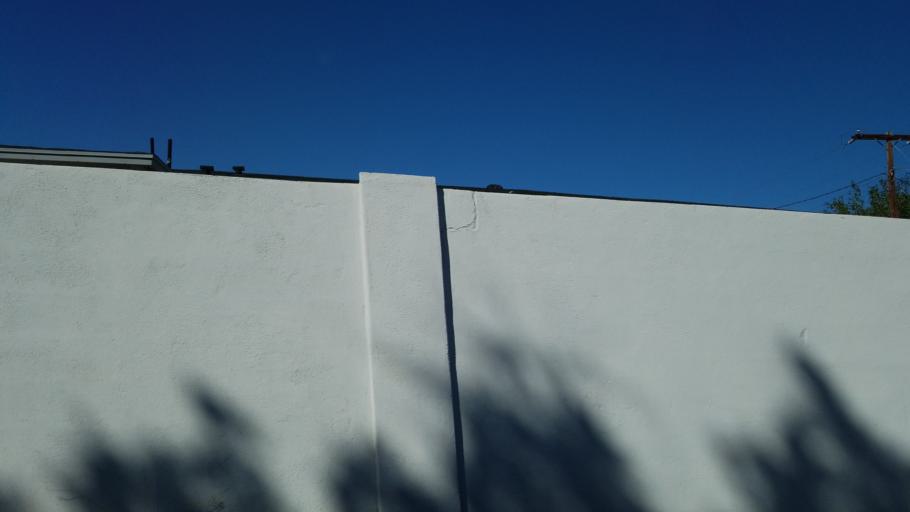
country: US
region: Arizona
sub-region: Maricopa County
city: Glendale
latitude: 33.5443
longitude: -112.1774
